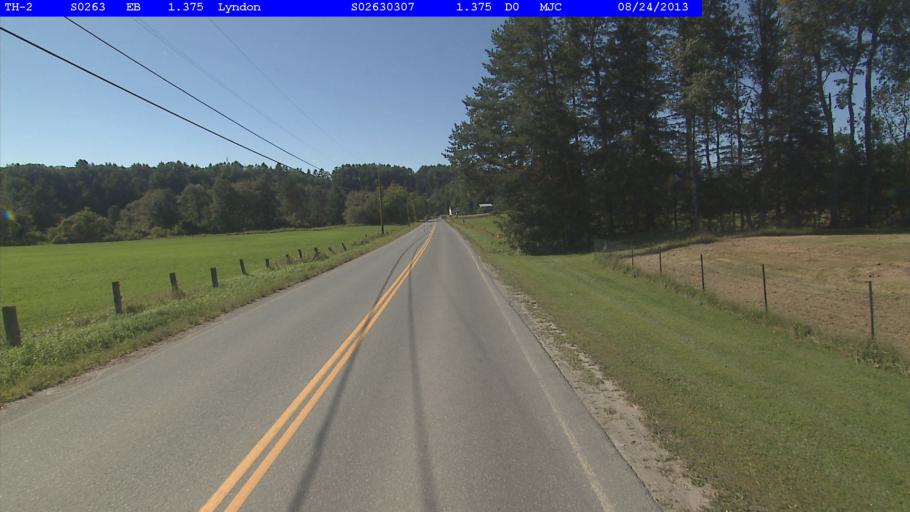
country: US
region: Vermont
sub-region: Caledonia County
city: Lyndon
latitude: 44.5059
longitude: -71.9878
